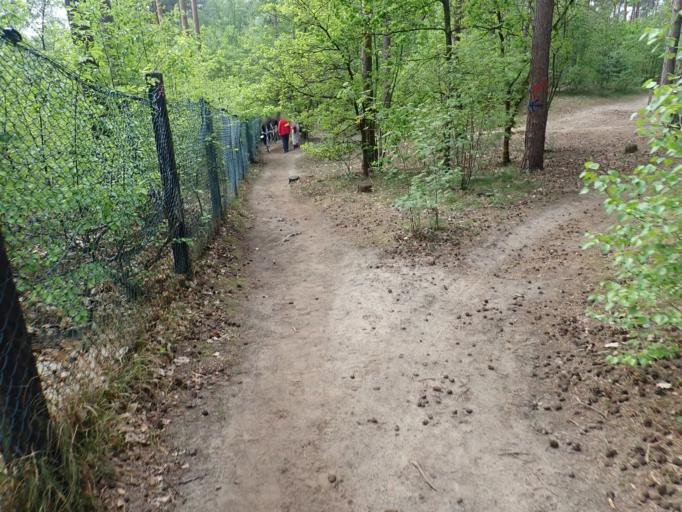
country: BE
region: Flanders
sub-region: Provincie Antwerpen
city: Herentals
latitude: 51.1943
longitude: 4.8447
